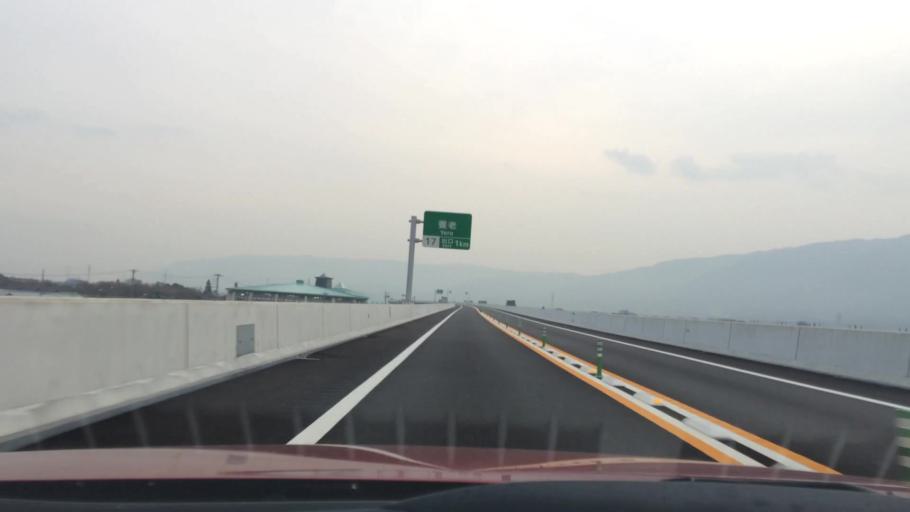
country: JP
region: Gifu
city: Ogaki
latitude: 35.3022
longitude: 136.5781
